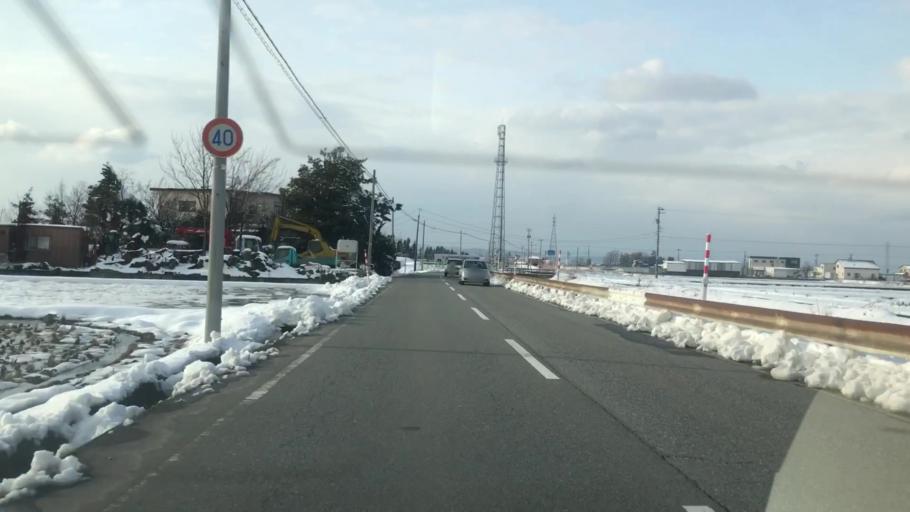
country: JP
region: Toyama
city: Toyama-shi
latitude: 36.6390
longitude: 137.2610
